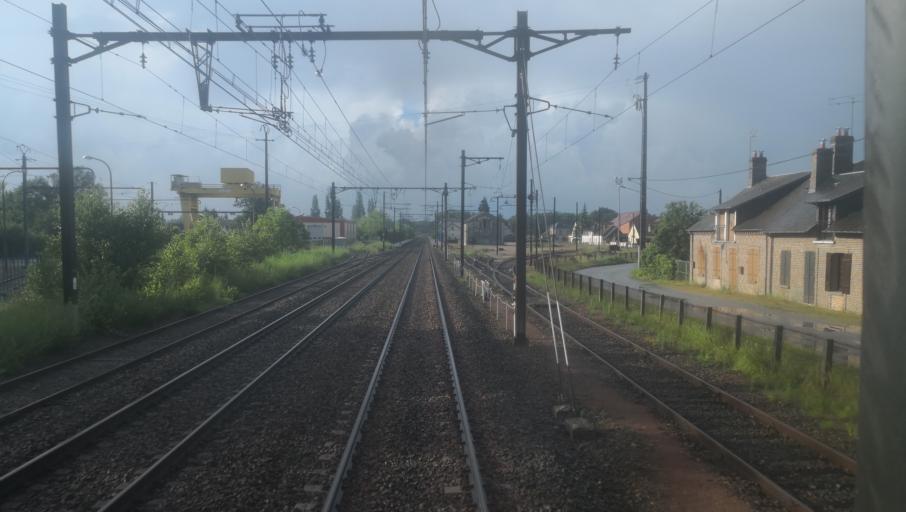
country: FR
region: Centre
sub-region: Departement du Loiret
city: La Ferte-Saint-Aubin
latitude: 47.7181
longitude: 1.9330
